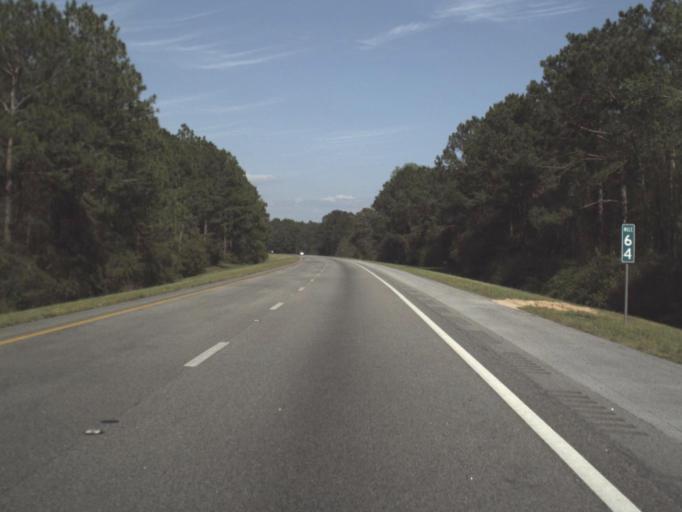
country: US
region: Florida
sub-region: Okaloosa County
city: Crestview
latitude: 30.7171
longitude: -86.4410
